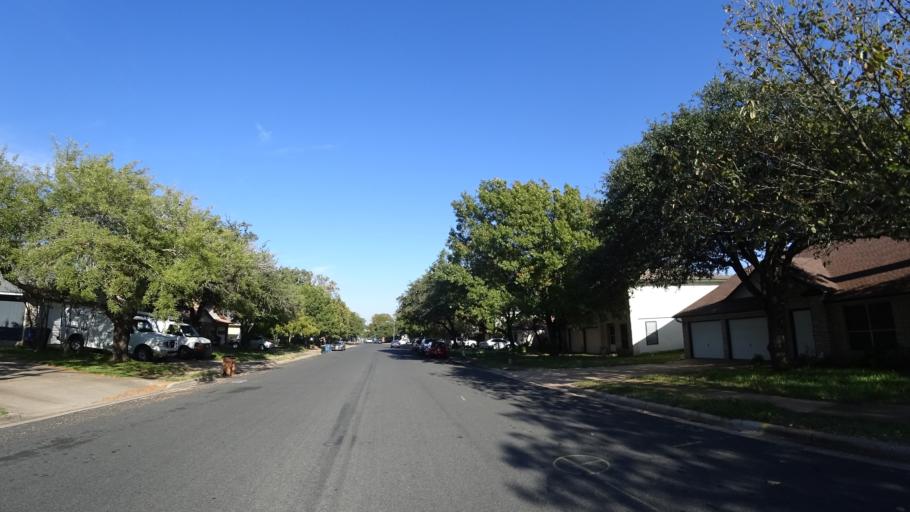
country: US
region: Texas
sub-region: Travis County
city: Shady Hollow
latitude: 30.2055
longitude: -97.8526
